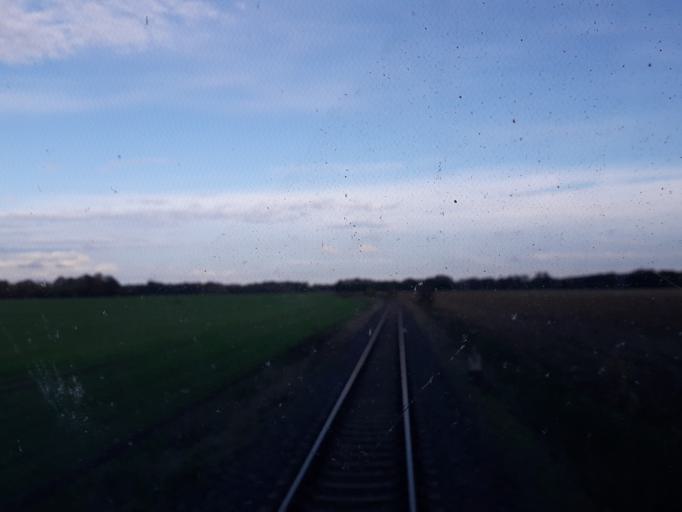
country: DE
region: Brandenburg
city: Gross Pankow
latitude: 53.0917
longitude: 11.9608
